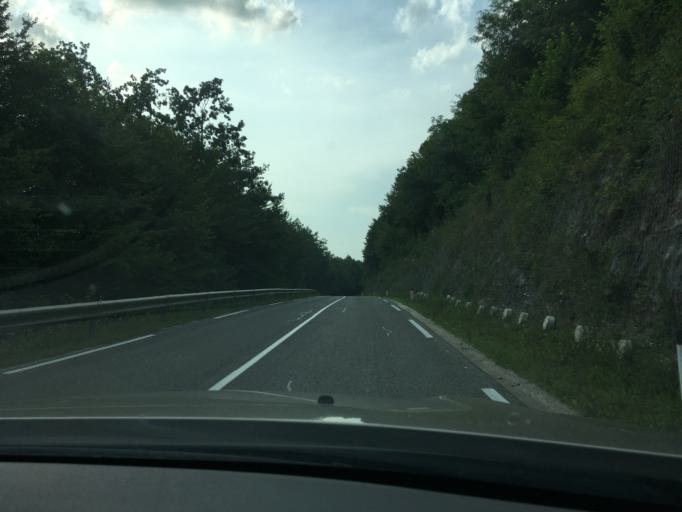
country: SI
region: Zuzemberk
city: Zuzemberk
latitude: 45.7892
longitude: 14.9904
